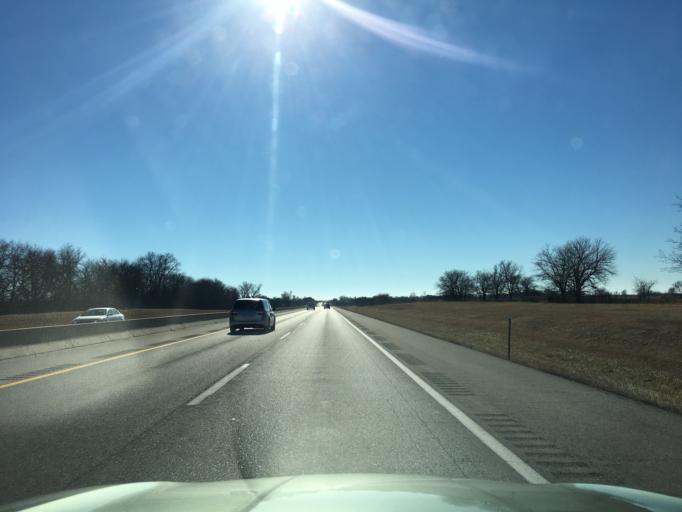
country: US
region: Kansas
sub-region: Sumner County
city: Wellington
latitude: 37.0967
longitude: -97.3387
